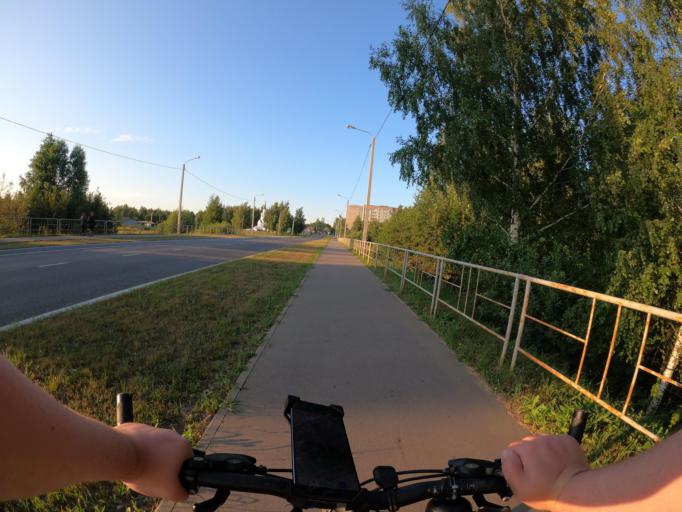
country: RU
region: Moskovskaya
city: Beloozerskiy
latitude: 55.4598
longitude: 38.4307
